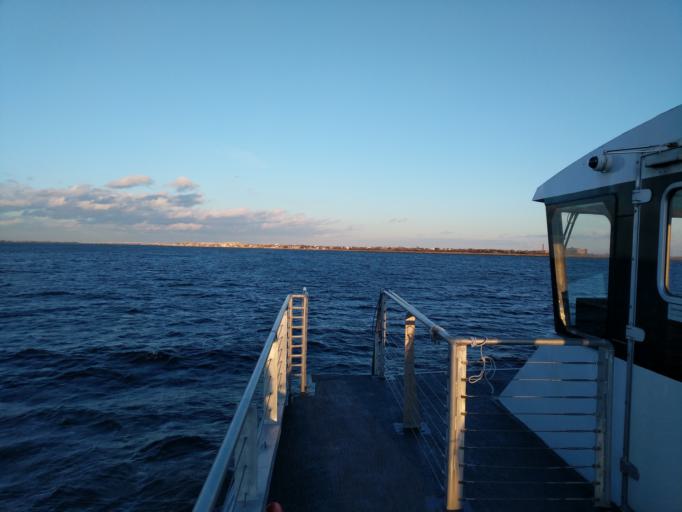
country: US
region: New York
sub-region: Kings County
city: East New York
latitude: 40.5747
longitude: -73.8824
